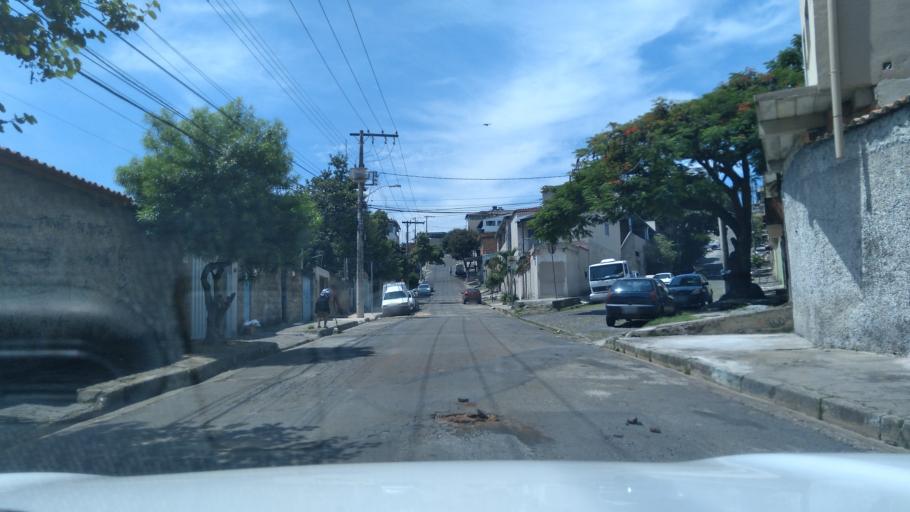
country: BR
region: Minas Gerais
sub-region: Contagem
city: Contagem
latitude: -19.9110
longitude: -44.0231
